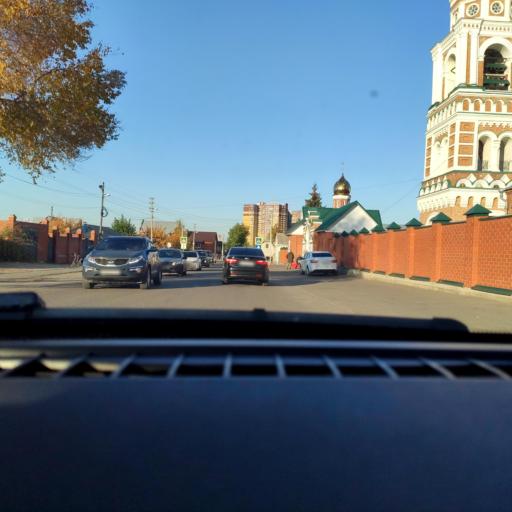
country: RU
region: Voronezj
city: Voronezh
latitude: 51.6997
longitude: 39.2683
